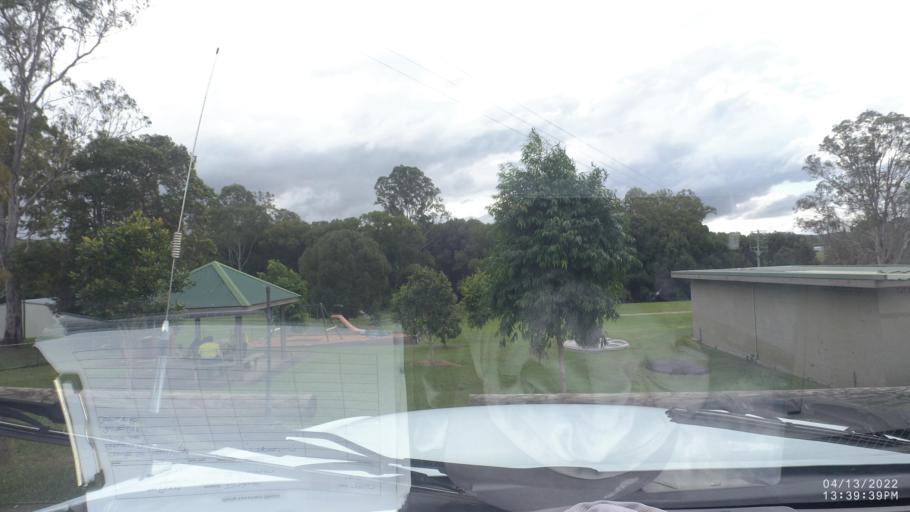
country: AU
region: Queensland
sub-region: Gold Coast
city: Ormeau Hills
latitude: -27.8272
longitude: 153.1794
